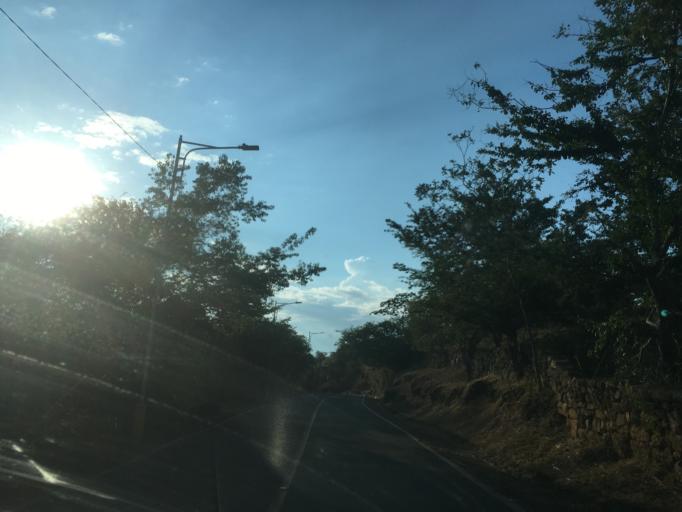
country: CO
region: Santander
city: Barichara
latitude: 6.6366
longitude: -73.2122
